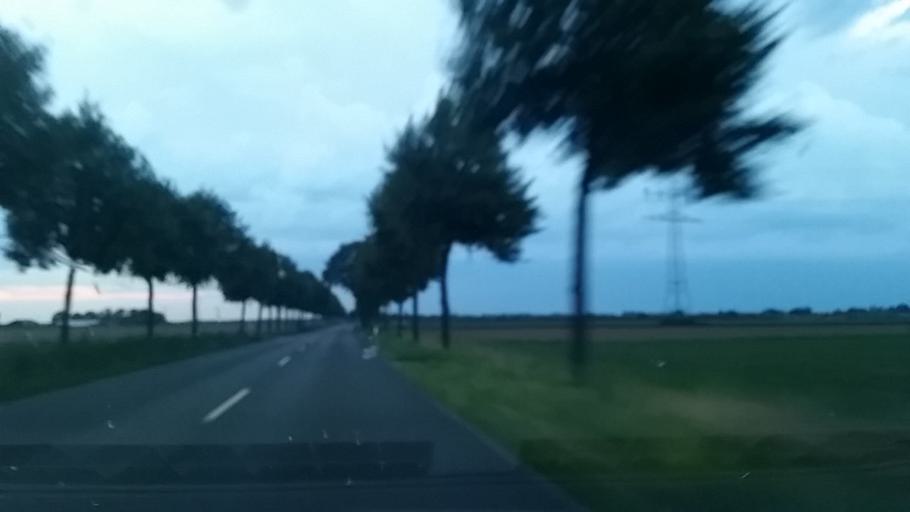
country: DE
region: North Rhine-Westphalia
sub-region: Regierungsbezirk Dusseldorf
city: Willich
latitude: 51.2539
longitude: 6.5808
